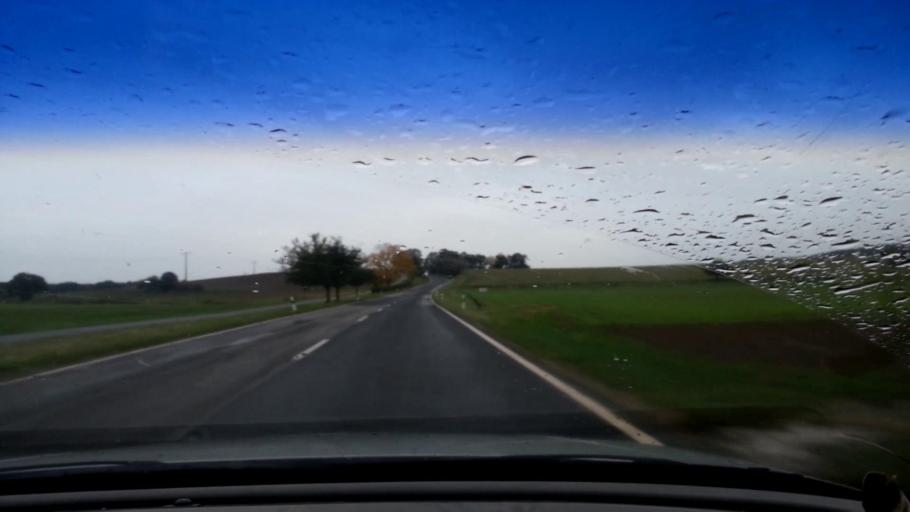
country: DE
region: Bavaria
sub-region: Upper Franconia
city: Burgebrach
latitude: 49.8516
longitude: 10.7098
